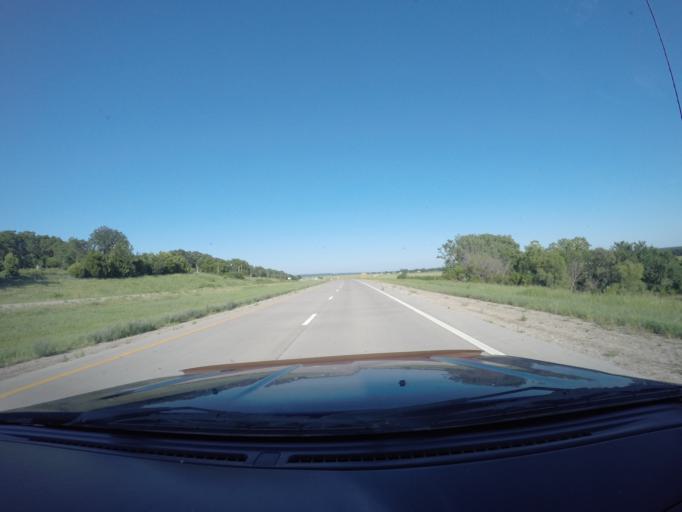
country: US
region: Kansas
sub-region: Shawnee County
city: Topeka
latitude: 39.0865
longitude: -95.4844
